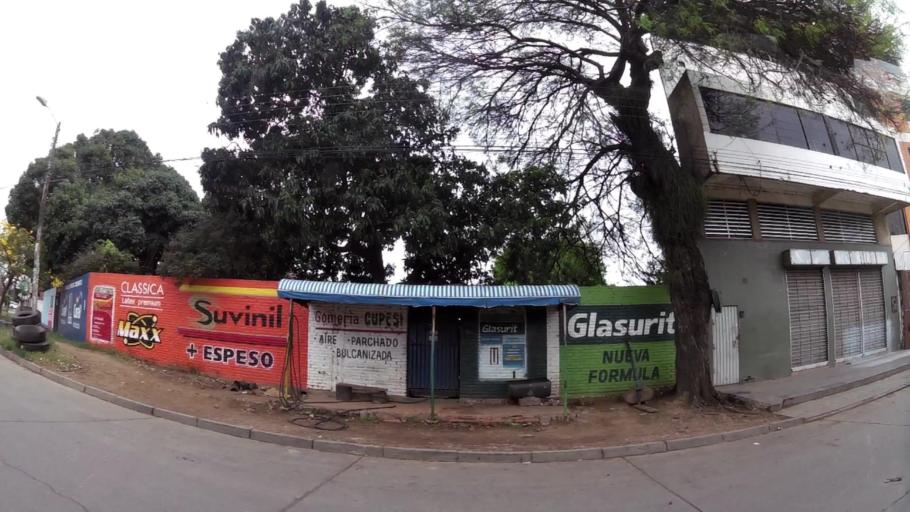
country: BO
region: Santa Cruz
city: Santa Cruz de la Sierra
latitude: -17.7857
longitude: -63.1608
